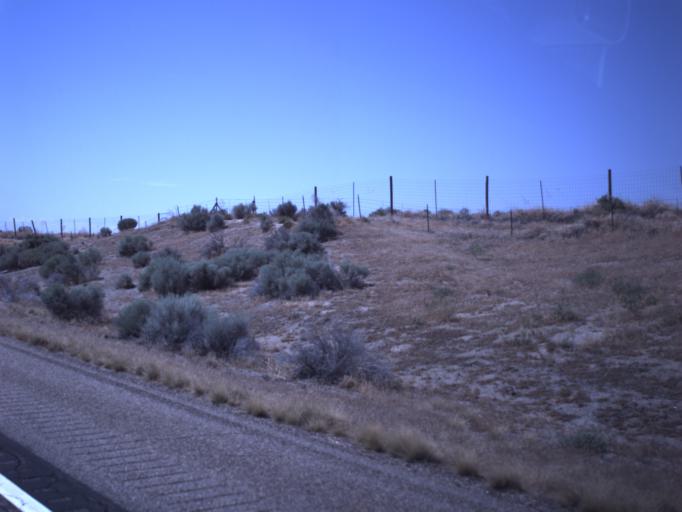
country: US
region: Utah
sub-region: Millard County
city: Delta
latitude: 39.3930
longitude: -112.5012
